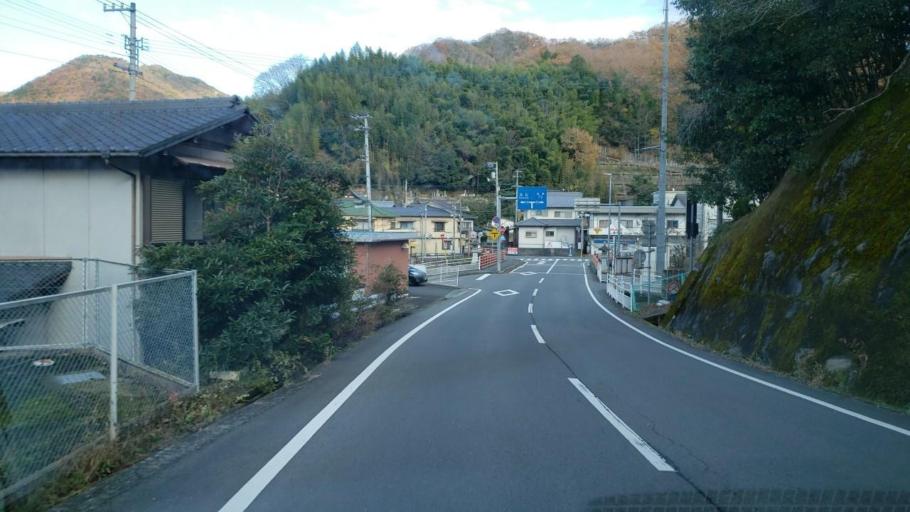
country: JP
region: Tokushima
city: Wakimachi
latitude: 34.1708
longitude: 134.0809
